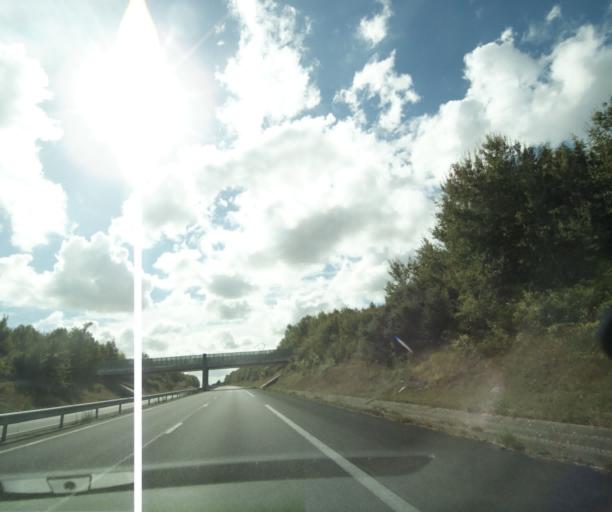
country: FR
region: Poitou-Charentes
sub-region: Departement de la Charente-Maritime
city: Saint-Georges-des-Coteaux
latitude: 45.8217
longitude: -0.7064
